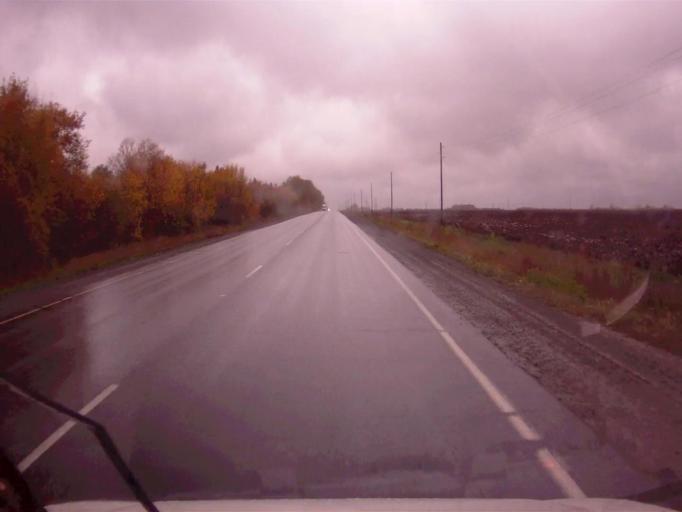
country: RU
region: Chelyabinsk
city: Argayash
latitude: 55.4277
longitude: 60.9977
